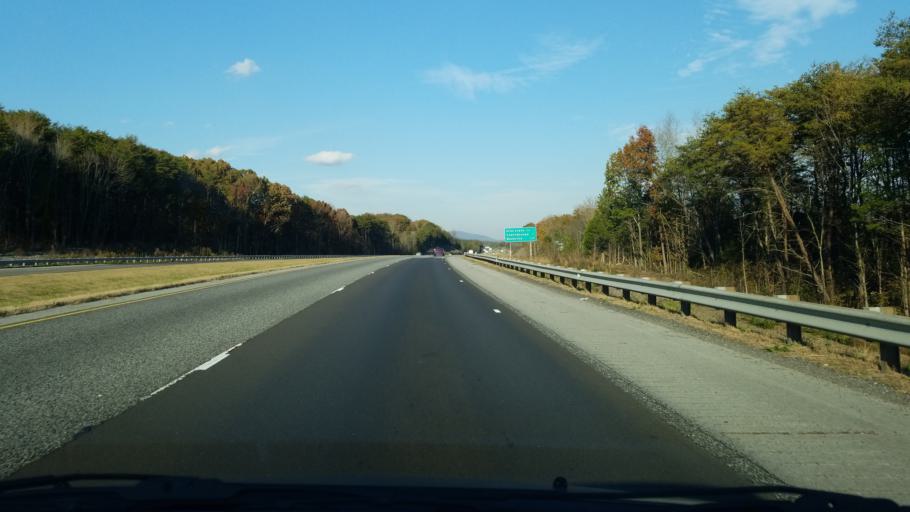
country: US
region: Georgia
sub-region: Dade County
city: Trenton
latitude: 34.8804
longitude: -85.5114
